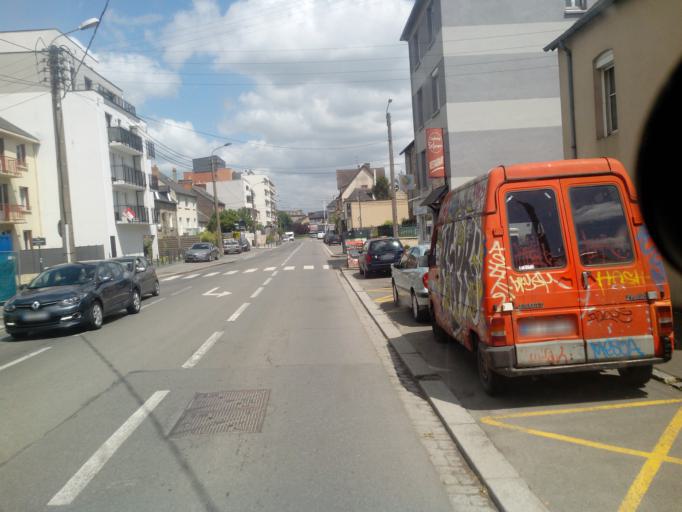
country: FR
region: Brittany
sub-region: Departement d'Ille-et-Vilaine
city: Rennes
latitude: 48.0964
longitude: -1.6925
